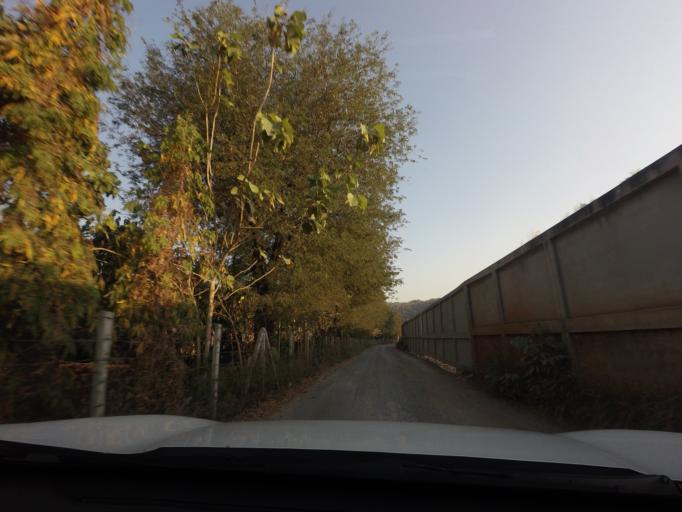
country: TH
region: Nakhon Ratchasima
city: Pak Chong
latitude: 14.6406
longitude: 101.3603
